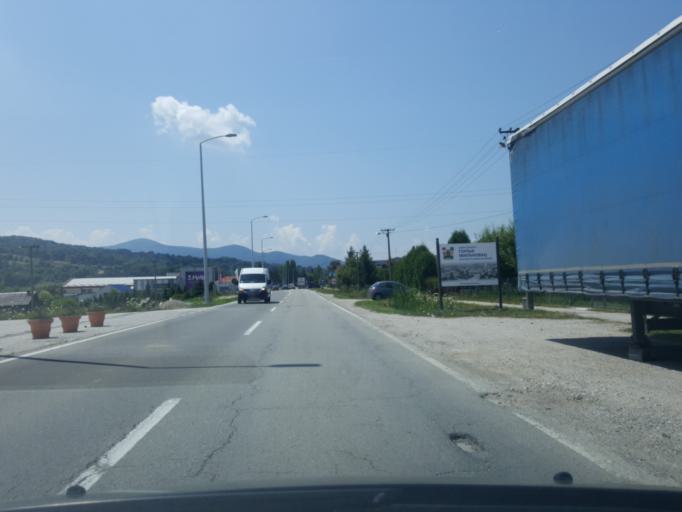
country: RS
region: Central Serbia
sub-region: Moravicki Okrug
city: Gornji Milanovac
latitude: 44.0442
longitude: 20.4865
